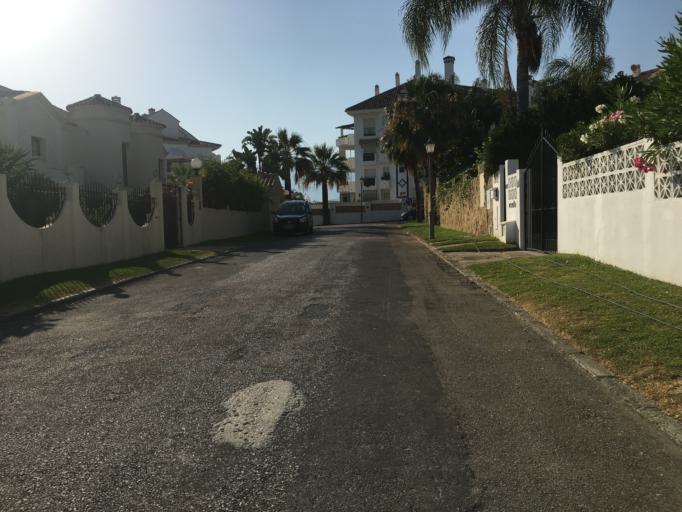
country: ES
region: Andalusia
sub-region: Provincia de Malaga
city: Marbella
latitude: 36.5016
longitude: -4.8141
